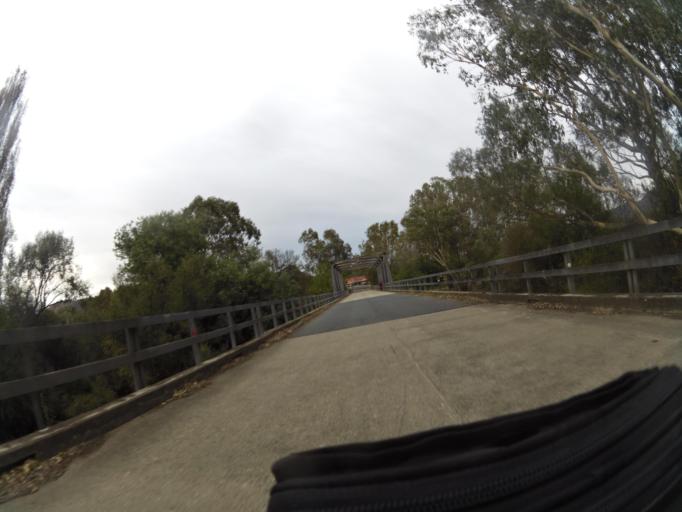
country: AU
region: New South Wales
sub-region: Greater Hume Shire
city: Holbrook
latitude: -36.0454
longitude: 147.9328
